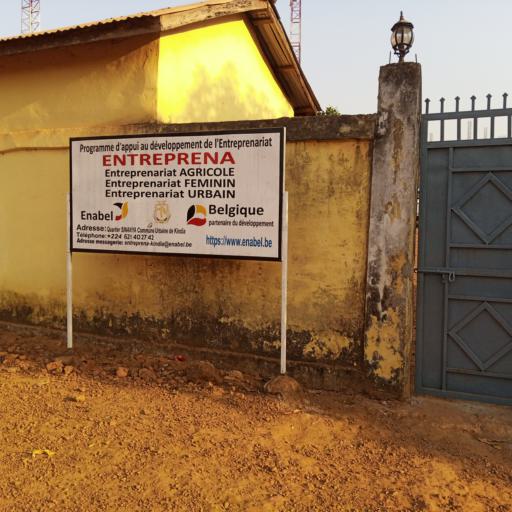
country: GN
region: Kindia
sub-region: Kindia
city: Kindia
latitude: 10.0383
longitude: -12.8676
